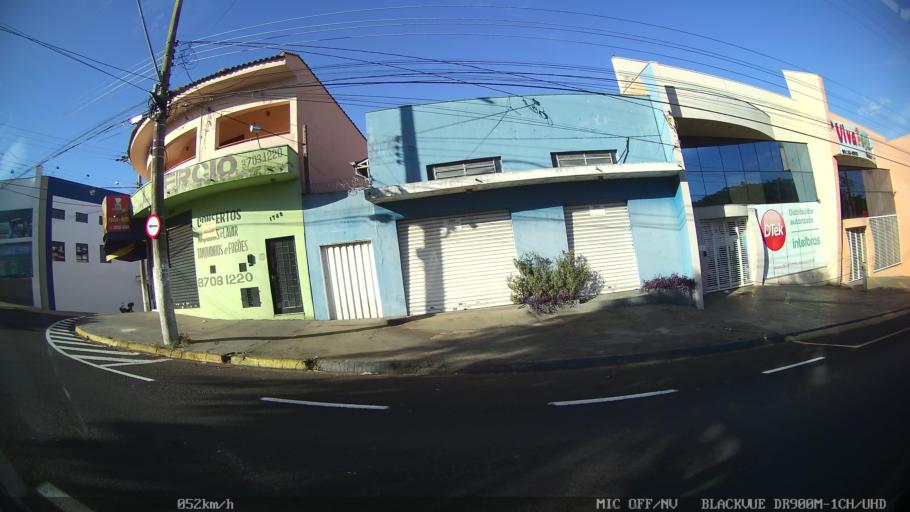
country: BR
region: Sao Paulo
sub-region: Franca
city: Franca
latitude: -20.5185
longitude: -47.3972
